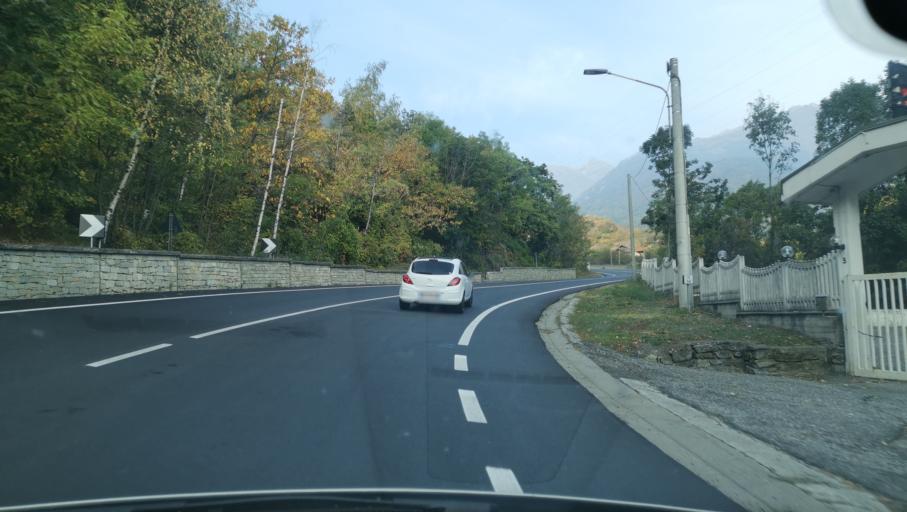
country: IT
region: Piedmont
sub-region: Provincia di Torino
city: Gravere
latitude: 45.1293
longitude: 7.0301
